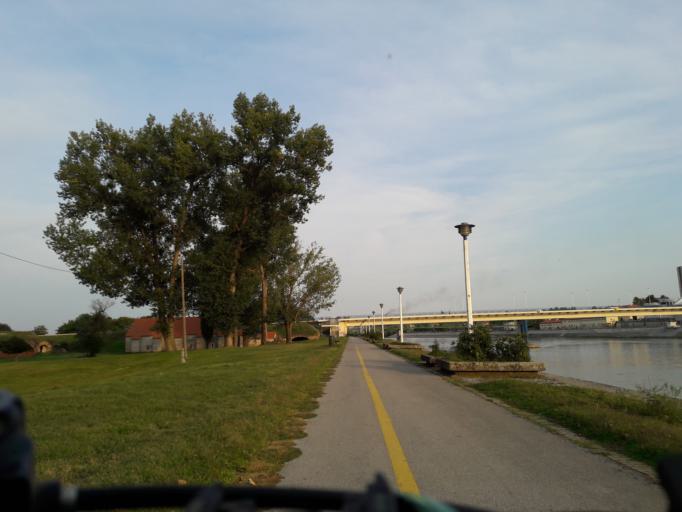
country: HR
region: Osjecko-Baranjska
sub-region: Grad Osijek
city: Osijek
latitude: 45.5638
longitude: 18.6996
